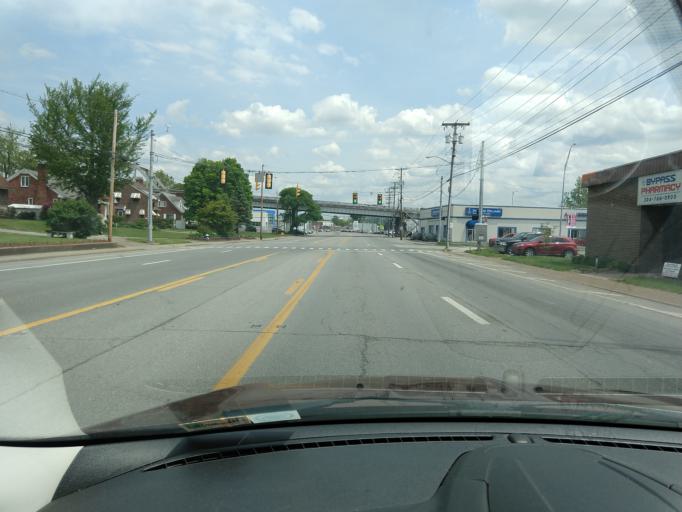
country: US
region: West Virginia
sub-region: Kanawha County
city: Dunbar
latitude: 38.3538
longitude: -81.7381
